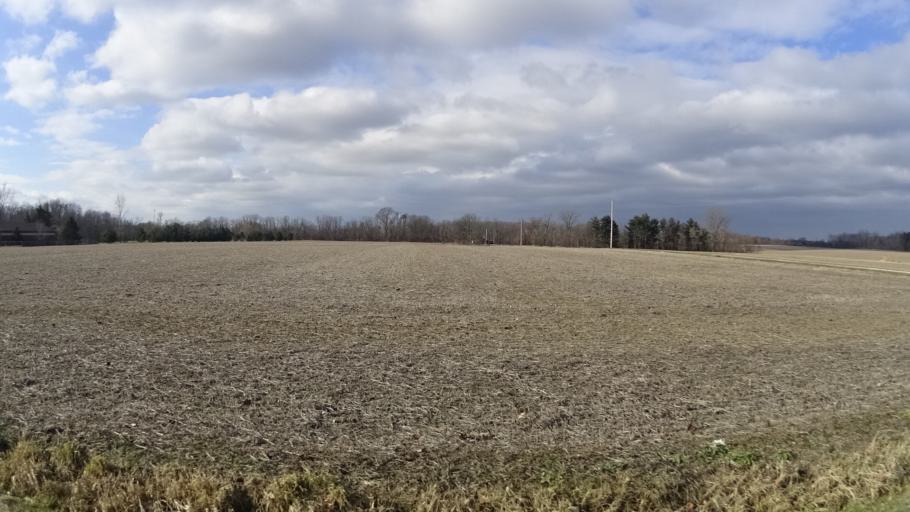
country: US
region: Ohio
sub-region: Lorain County
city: Camden
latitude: 41.2640
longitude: -82.2892
